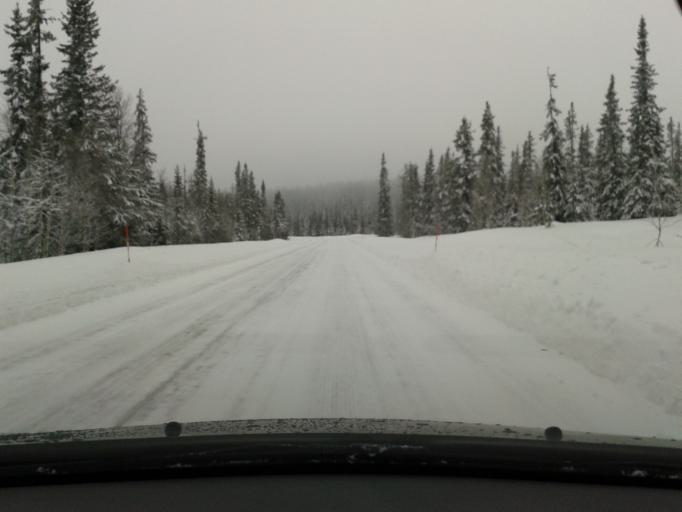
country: SE
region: Vaesterbotten
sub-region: Vilhelmina Kommun
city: Sjoberg
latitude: 65.1055
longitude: 15.8723
